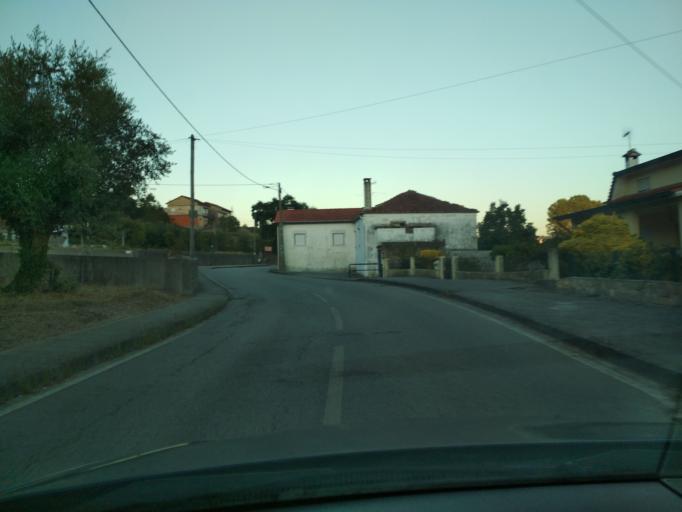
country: PT
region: Coimbra
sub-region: Condeixa-A-Nova
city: Condeixa-a-Nova
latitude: 40.1678
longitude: -8.4704
